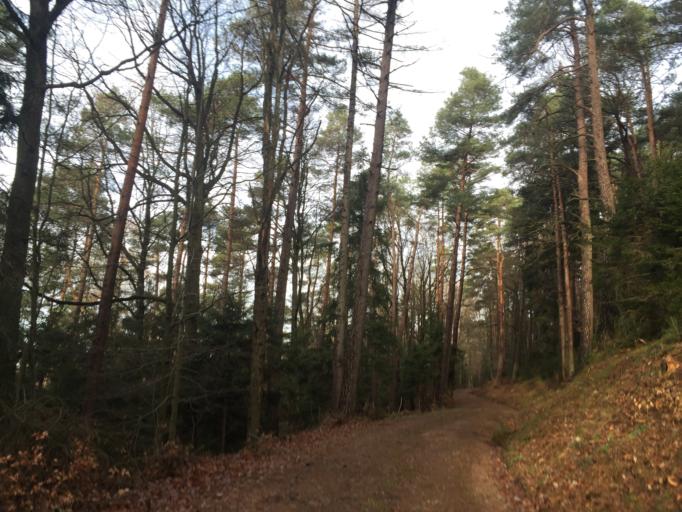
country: DE
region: Hesse
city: Reichelsheim
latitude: 49.6995
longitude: 8.8922
